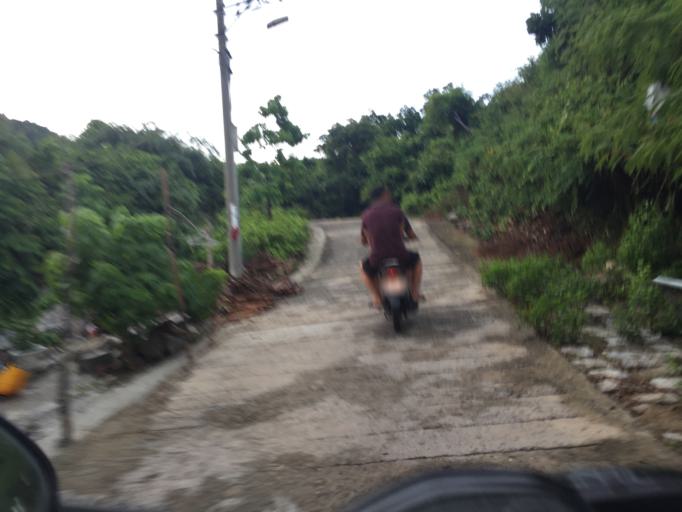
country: VN
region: Quang Nam
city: Hoi An
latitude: 15.9544
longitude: 108.5082
